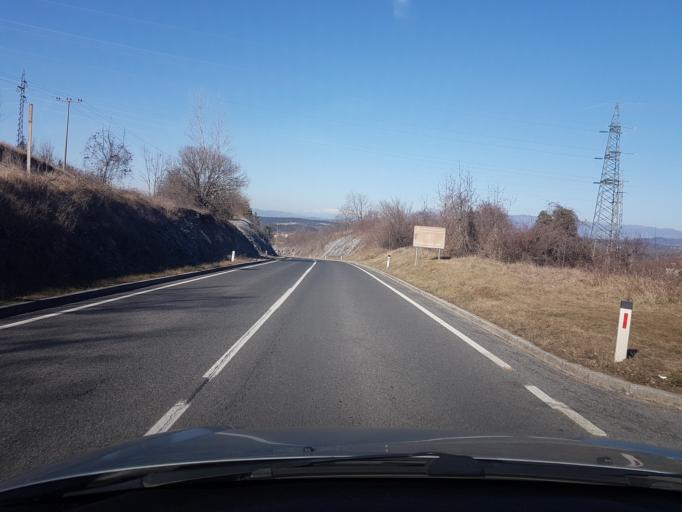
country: SI
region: Sezana
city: Sezana
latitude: 45.7119
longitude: 13.8754
